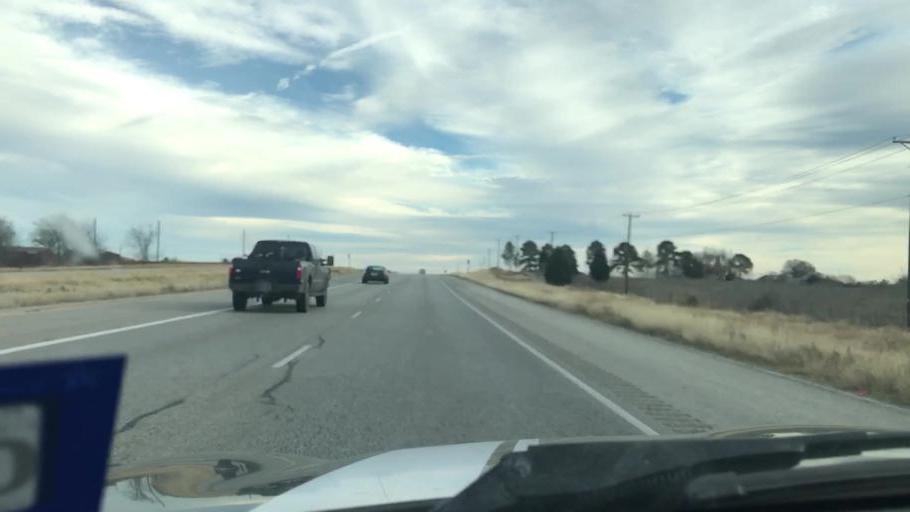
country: US
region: Texas
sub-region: Bastrop County
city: Elgin
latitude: 30.3156
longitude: -97.3114
